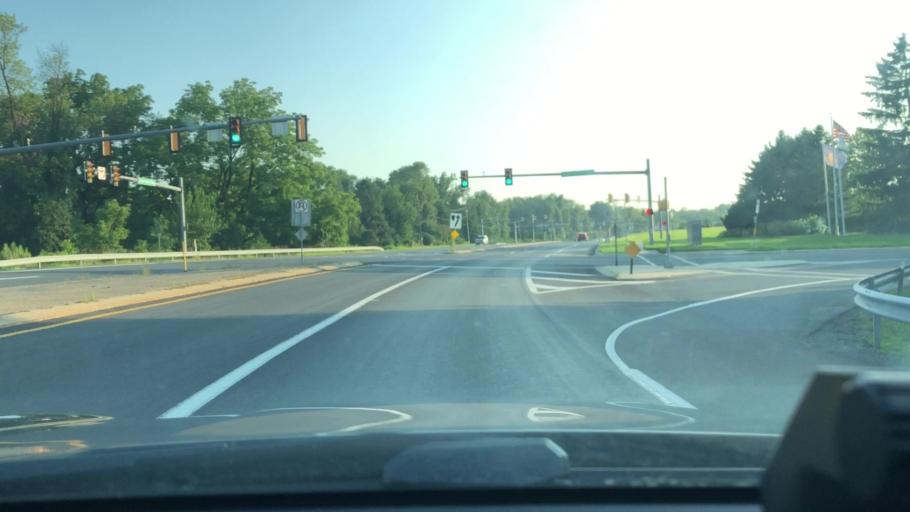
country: US
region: Pennsylvania
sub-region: Lehigh County
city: Coopersburg
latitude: 40.5510
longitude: -75.4205
